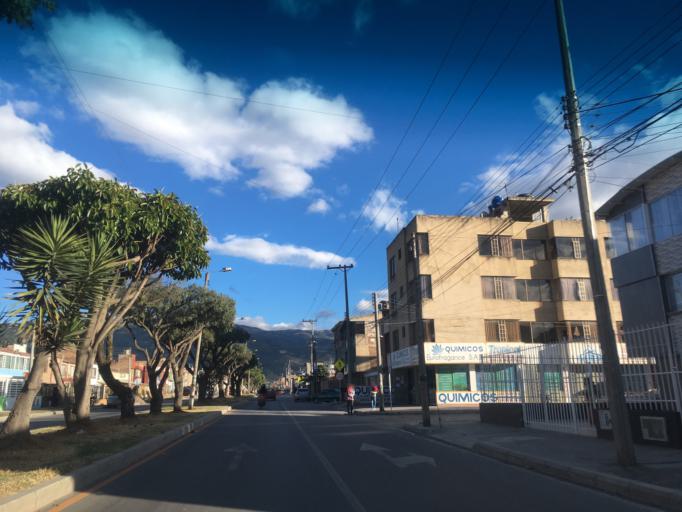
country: CO
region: Boyaca
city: Sogamoso
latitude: 5.7177
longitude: -72.9419
